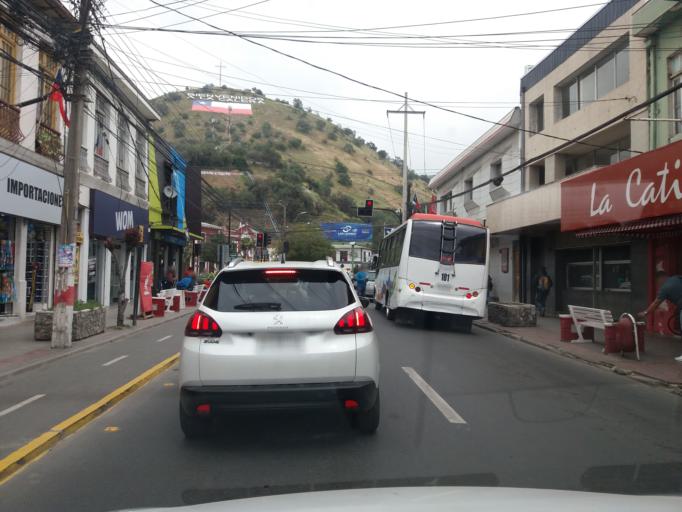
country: CL
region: Valparaiso
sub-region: Provincia de Quillota
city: Hacienda La Calera
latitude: -32.7887
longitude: -71.1895
